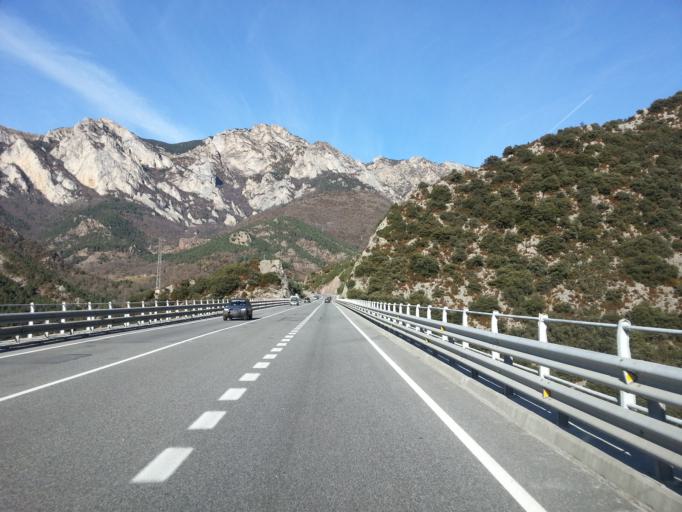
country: ES
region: Catalonia
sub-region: Provincia de Barcelona
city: Baga
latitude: 42.2742
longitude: 1.8535
